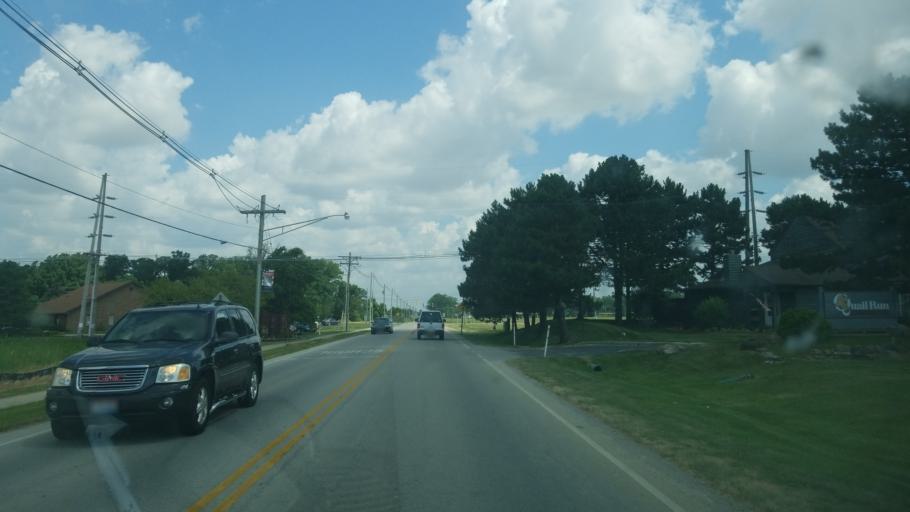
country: US
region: Ohio
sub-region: Auglaize County
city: Wapakoneta
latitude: 40.5836
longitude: -84.2028
